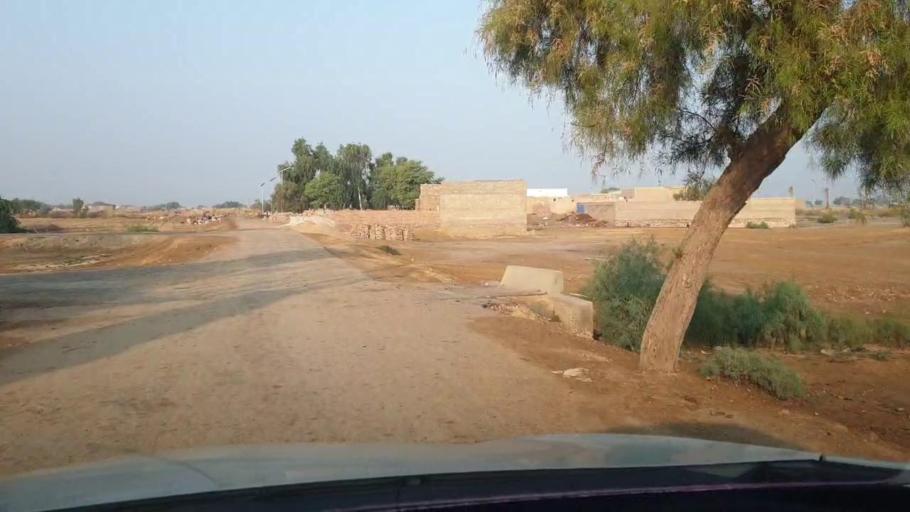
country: PK
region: Sindh
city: Sehwan
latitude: 26.3541
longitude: 67.7618
